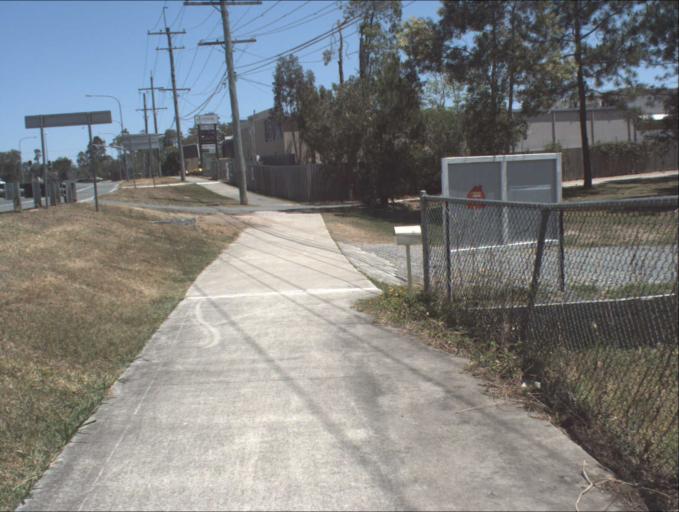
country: AU
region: Queensland
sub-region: Logan
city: Slacks Creek
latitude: -27.6727
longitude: 153.1856
